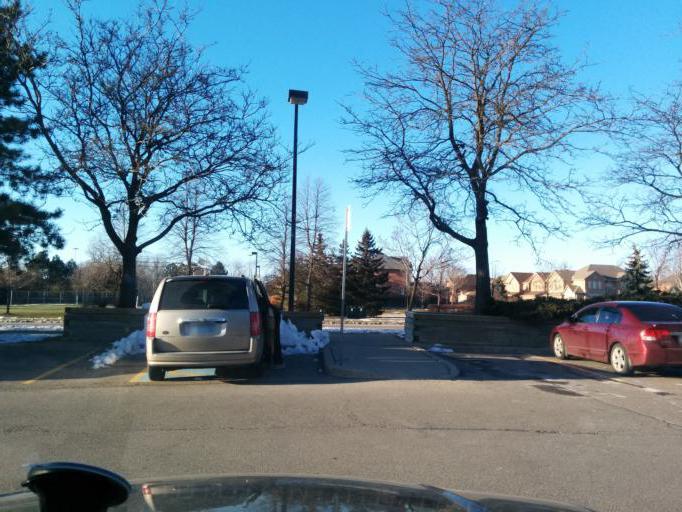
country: CA
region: Ontario
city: Mississauga
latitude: 43.5786
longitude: -79.6608
